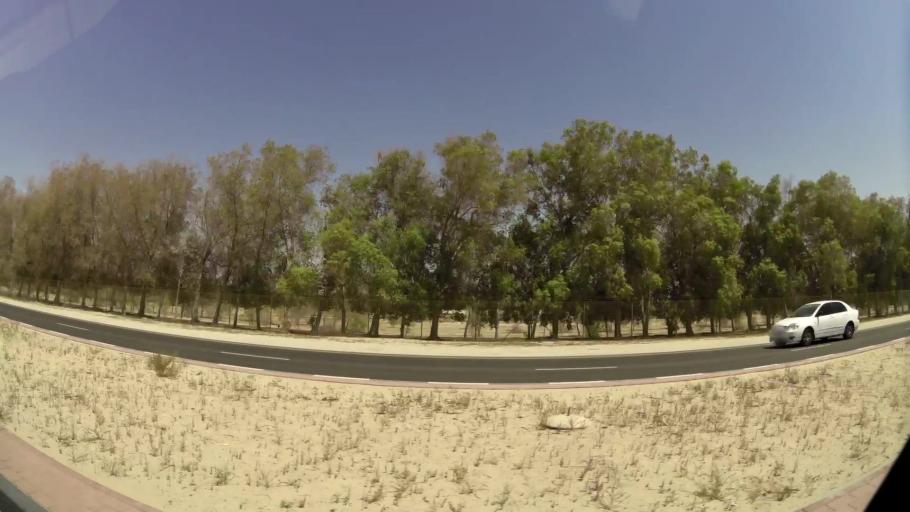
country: AE
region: Dubai
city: Dubai
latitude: 25.1288
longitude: 55.1902
